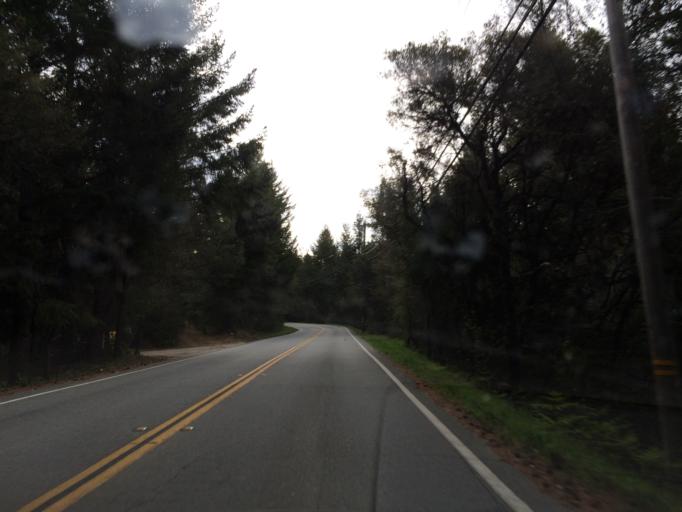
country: US
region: California
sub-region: Santa Cruz County
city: Bonny Doon
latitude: 37.0569
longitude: -122.1224
